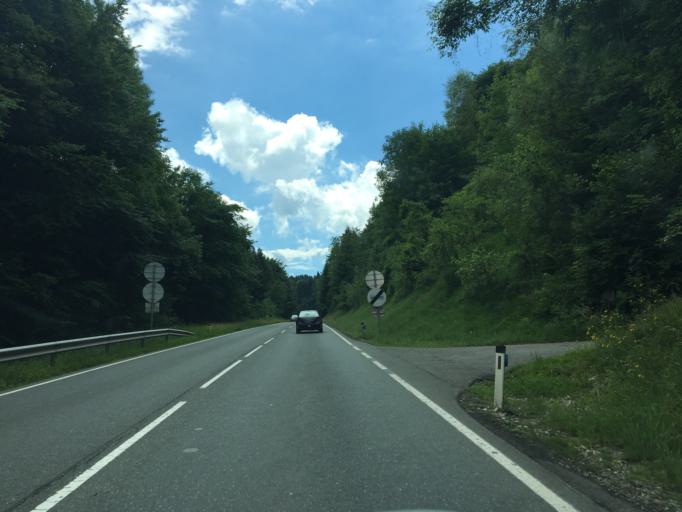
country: AT
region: Salzburg
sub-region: Politischer Bezirk Salzburg-Umgebung
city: Plainfeld
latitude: 47.8328
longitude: 13.1976
